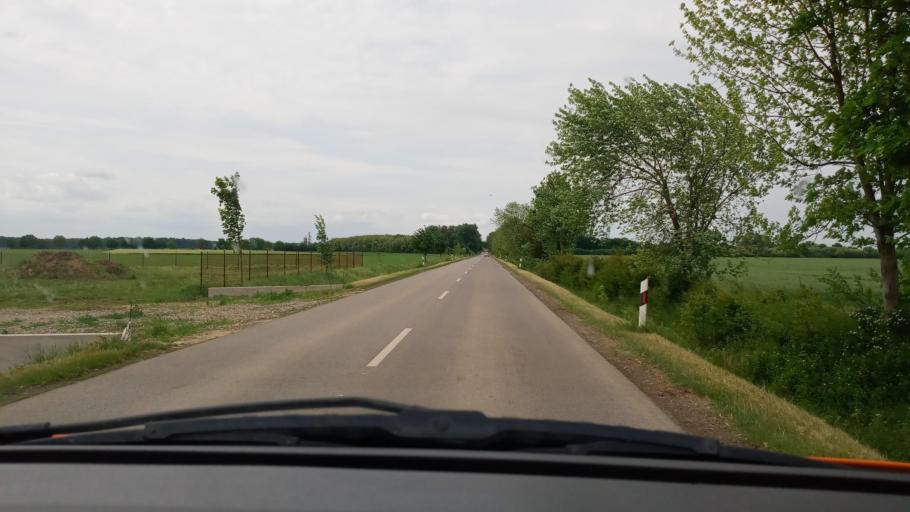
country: HU
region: Baranya
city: Vajszlo
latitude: 45.9123
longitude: 18.0510
